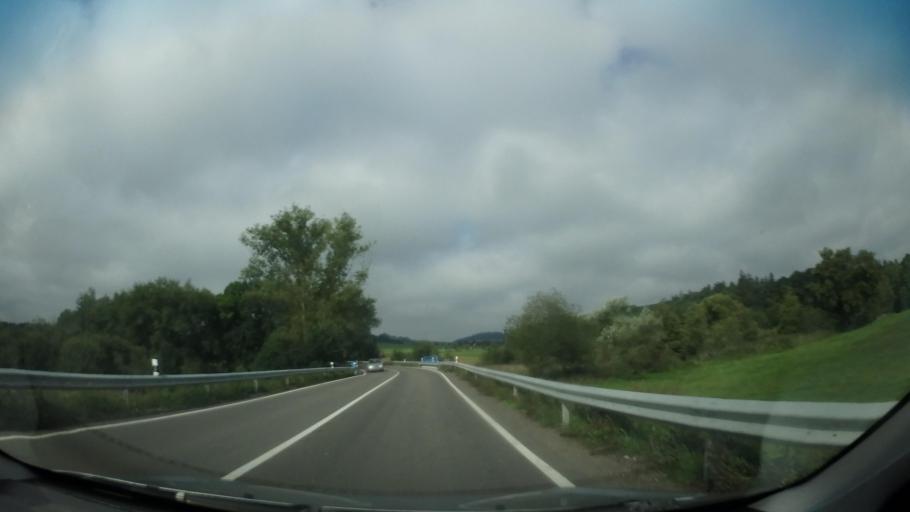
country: CZ
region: Central Bohemia
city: Neveklov
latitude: 49.7528
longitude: 14.5285
